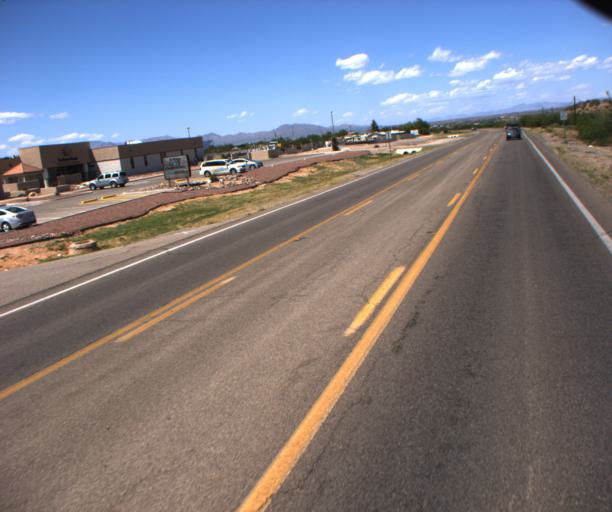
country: US
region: Arizona
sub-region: Cochise County
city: Benson
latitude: 31.9521
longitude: -110.2860
